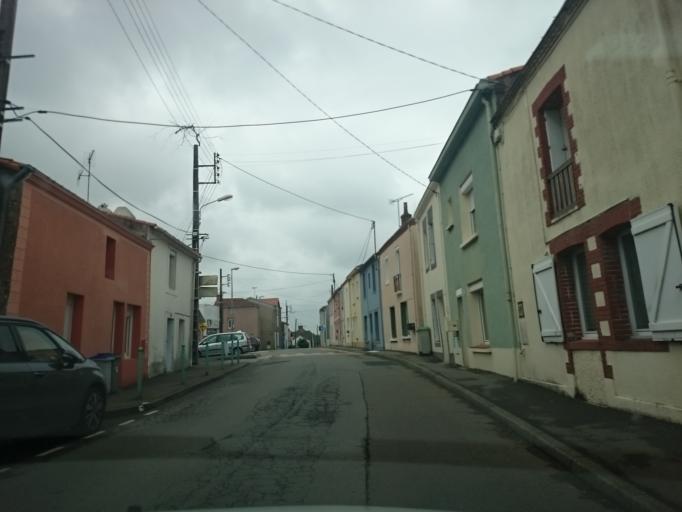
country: FR
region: Pays de la Loire
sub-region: Departement de la Loire-Atlantique
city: La Montagne
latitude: 47.1896
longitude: -1.6915
